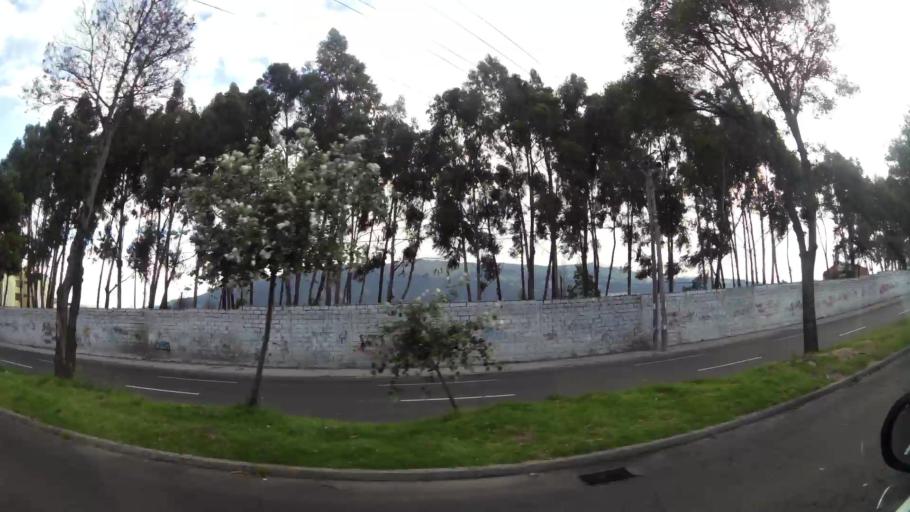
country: EC
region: Pichincha
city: Quito
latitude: -0.1346
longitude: -78.4733
